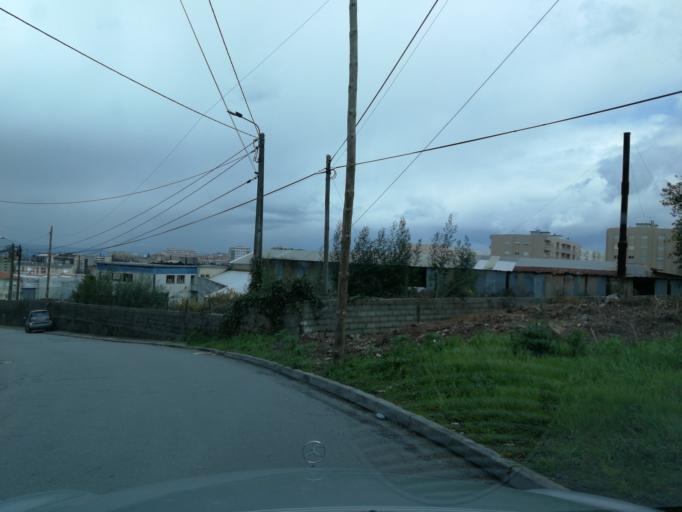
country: PT
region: Braga
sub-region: Braga
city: Braga
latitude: 41.5356
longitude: -8.4283
